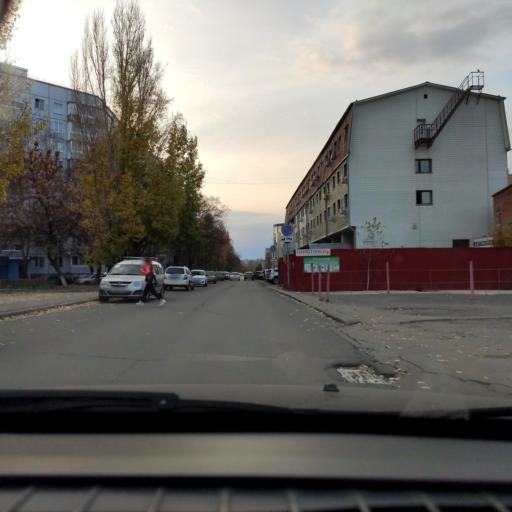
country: RU
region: Samara
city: Tol'yatti
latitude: 53.5327
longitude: 49.3234
